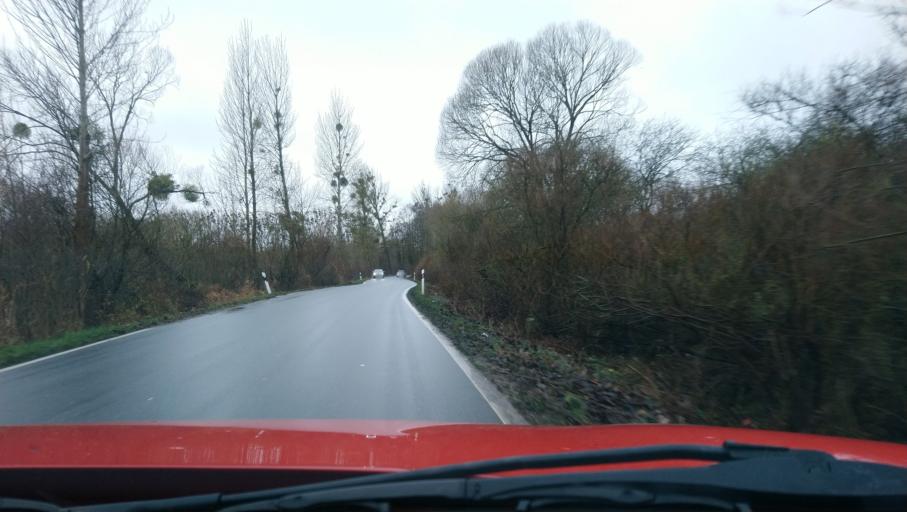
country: DE
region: Mecklenburg-Vorpommern
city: Seehof
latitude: 53.6785
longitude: 11.4470
